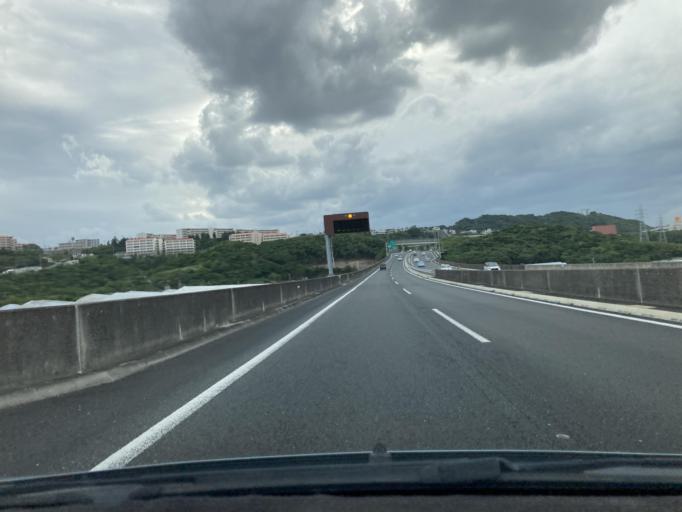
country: JP
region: Okinawa
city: Tomigusuku
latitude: 26.1738
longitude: 127.7026
